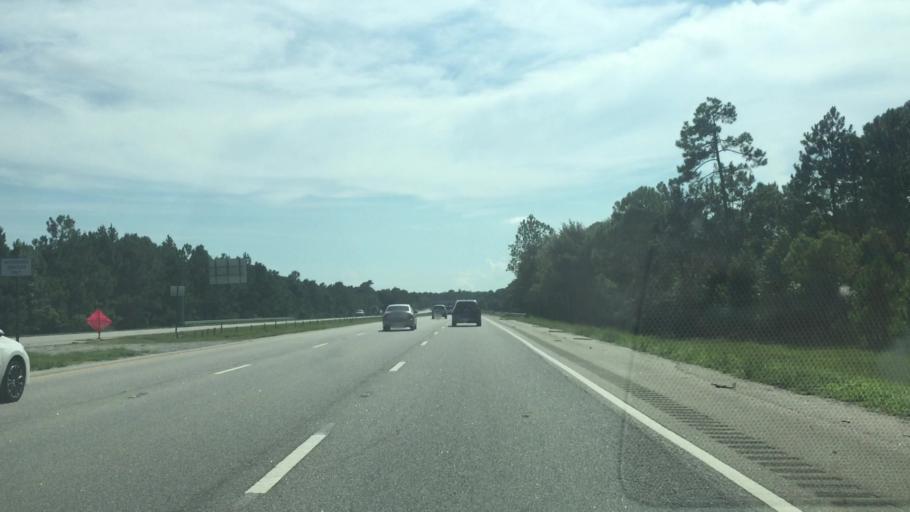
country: US
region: South Carolina
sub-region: Horry County
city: North Myrtle Beach
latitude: 33.8321
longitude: -78.7161
